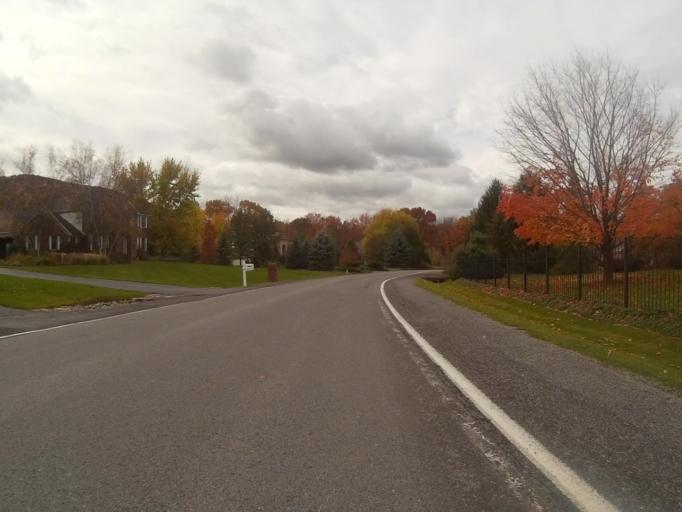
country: US
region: Pennsylvania
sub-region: Centre County
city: Boalsburg
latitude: 40.7736
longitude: -77.7588
